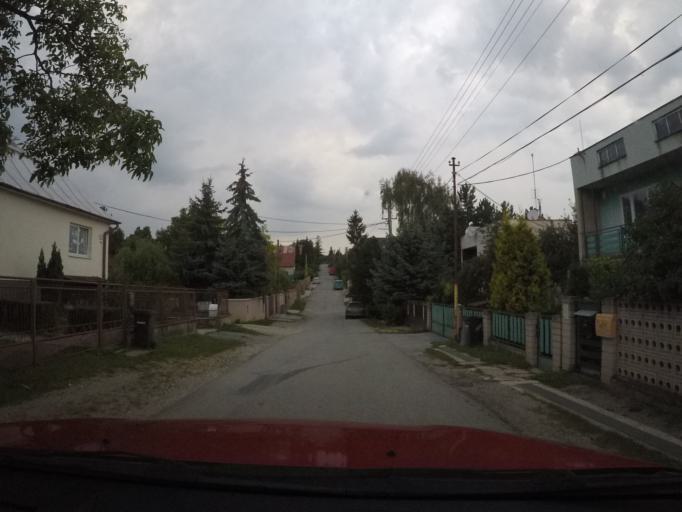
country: SK
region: Kosicky
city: Kosice
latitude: 48.6905
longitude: 21.2128
